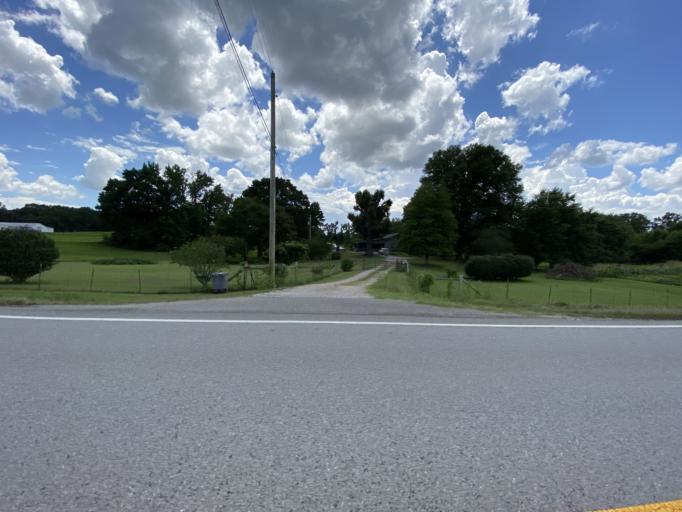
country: US
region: Alabama
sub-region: Lauderdale County
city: Underwood-Petersville
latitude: 34.9439
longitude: -87.8602
